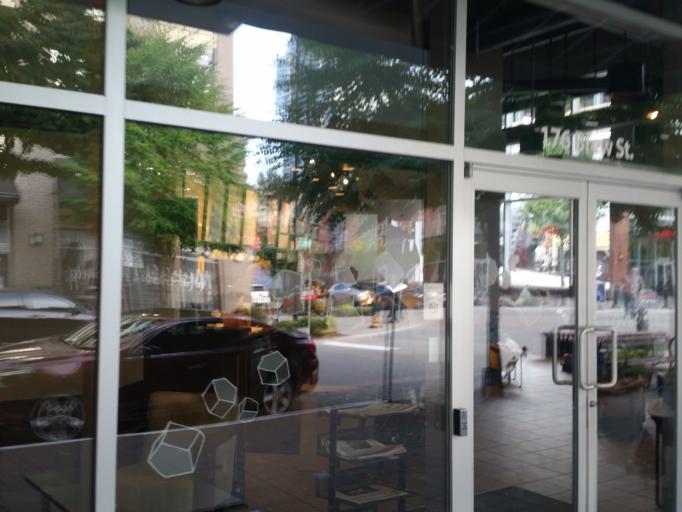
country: CA
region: British Columbia
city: Port Moody
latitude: 49.2796
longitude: -122.8285
